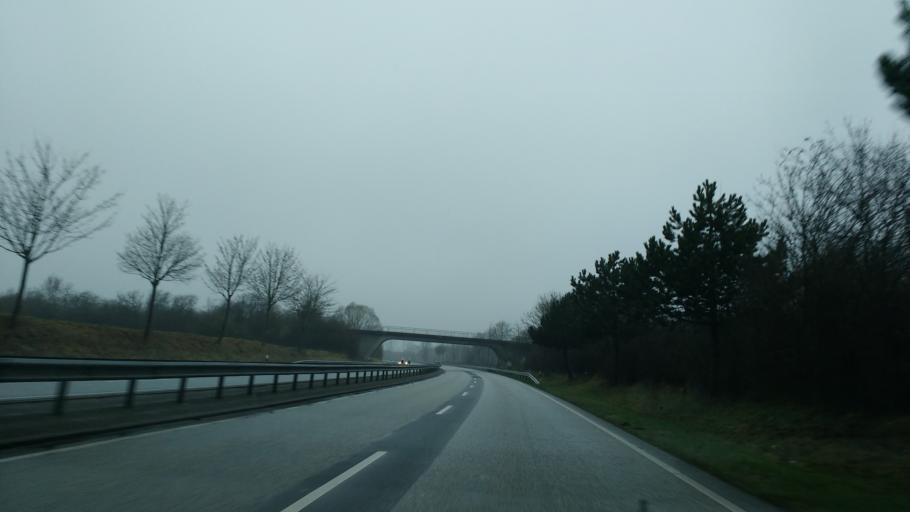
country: DE
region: Schleswig-Holstein
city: Jevenstedt
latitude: 54.2357
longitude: 9.6778
